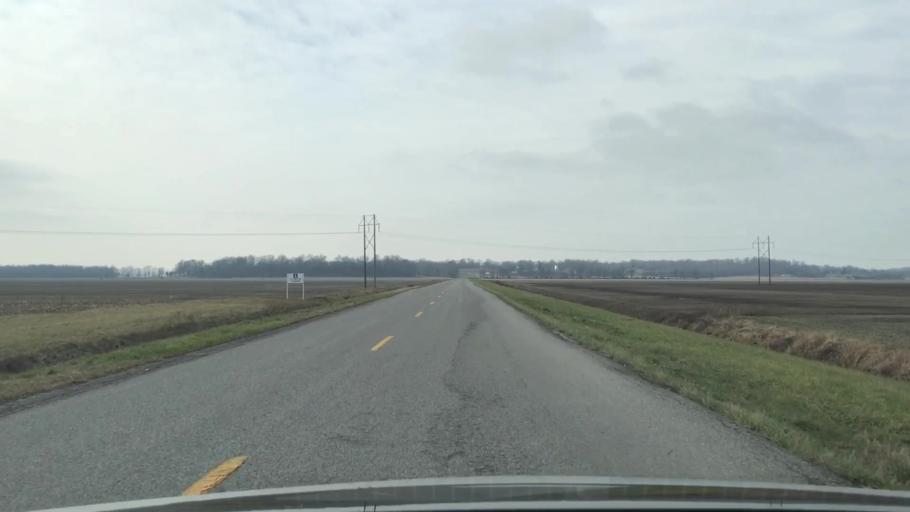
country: US
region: Kentucky
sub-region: McLean County
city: Calhoun
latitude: 37.5241
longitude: -87.3712
